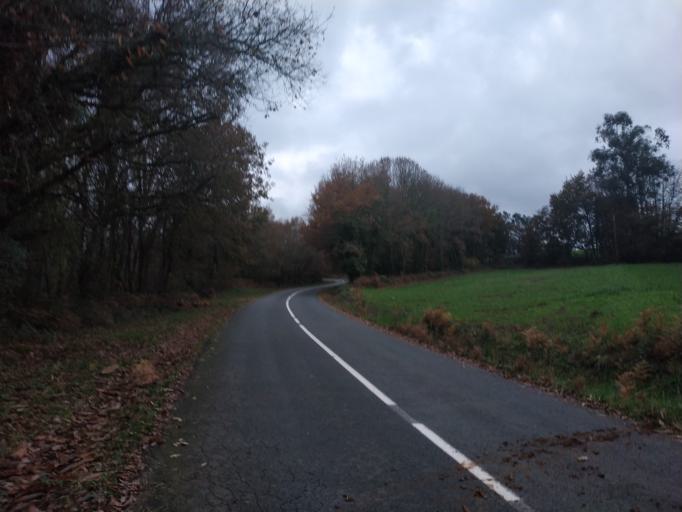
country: ES
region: Galicia
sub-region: Provincia de Pontevedra
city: Silleda
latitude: 42.7777
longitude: -8.1772
